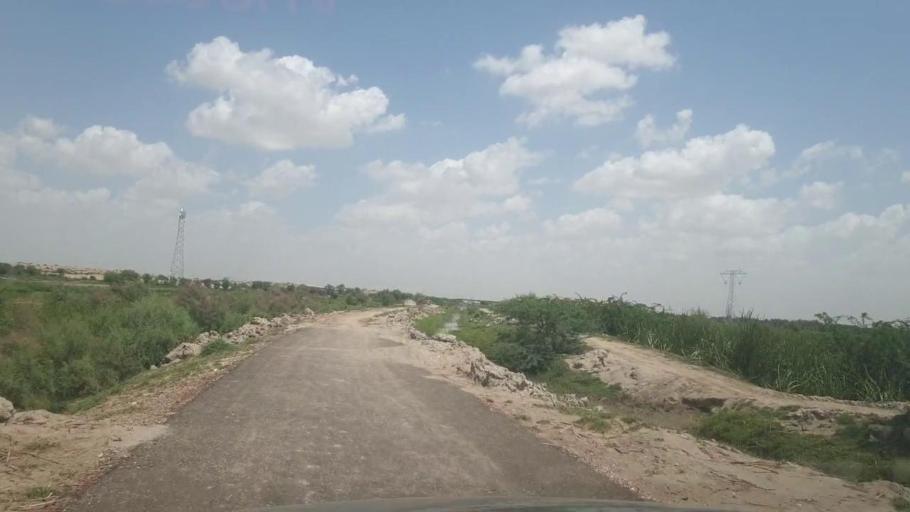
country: PK
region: Sindh
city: Kot Diji
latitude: 27.2333
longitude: 69.0406
